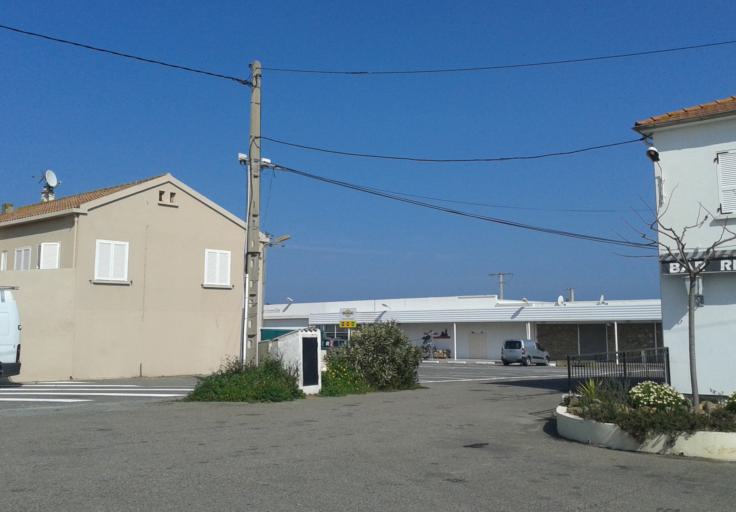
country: FR
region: Corsica
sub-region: Departement de la Haute-Corse
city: Linguizzetta
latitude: 42.2634
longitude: 9.5486
